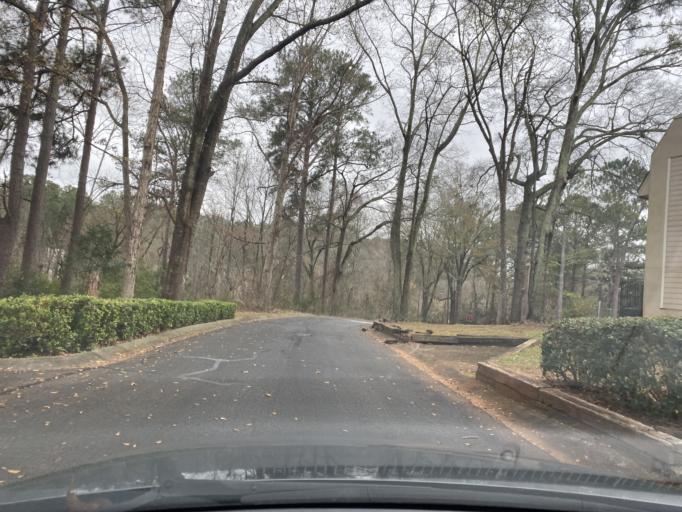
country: US
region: Georgia
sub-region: DeKalb County
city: Pine Mountain
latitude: 33.6969
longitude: -84.1452
